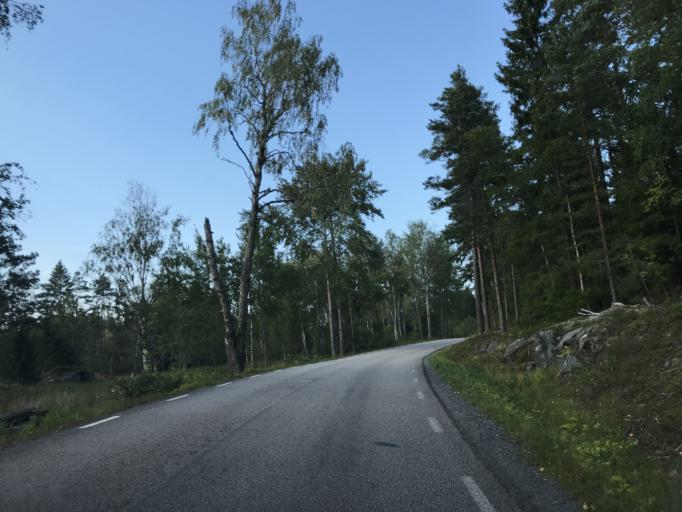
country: SE
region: Stockholm
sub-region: Norrtalje Kommun
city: Bjorko
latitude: 59.8714
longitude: 19.0127
